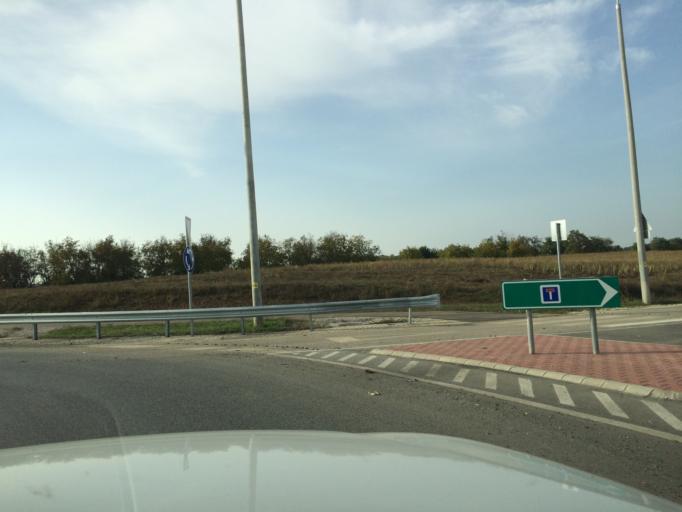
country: HU
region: Szabolcs-Szatmar-Bereg
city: Nyirtelek
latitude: 47.9572
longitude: 21.6525
